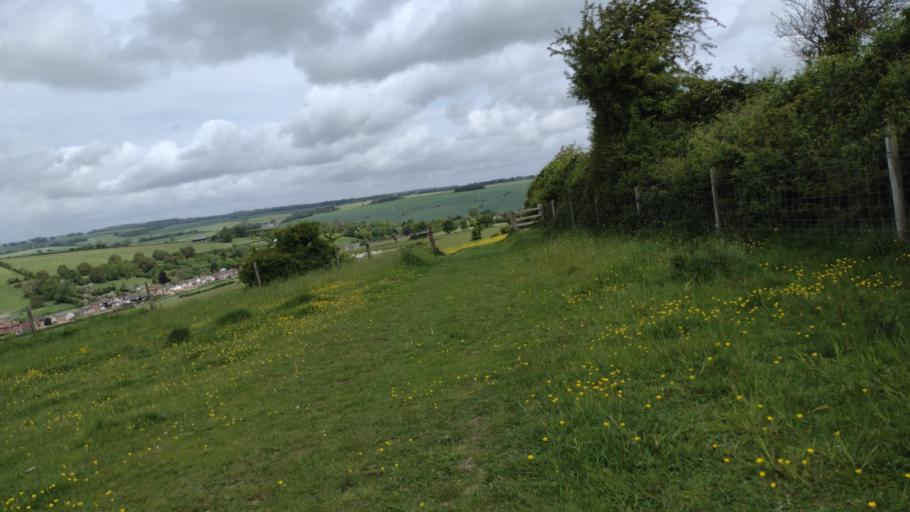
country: GB
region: England
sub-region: Wiltshire
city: Wilton
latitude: 51.0278
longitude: -1.8427
